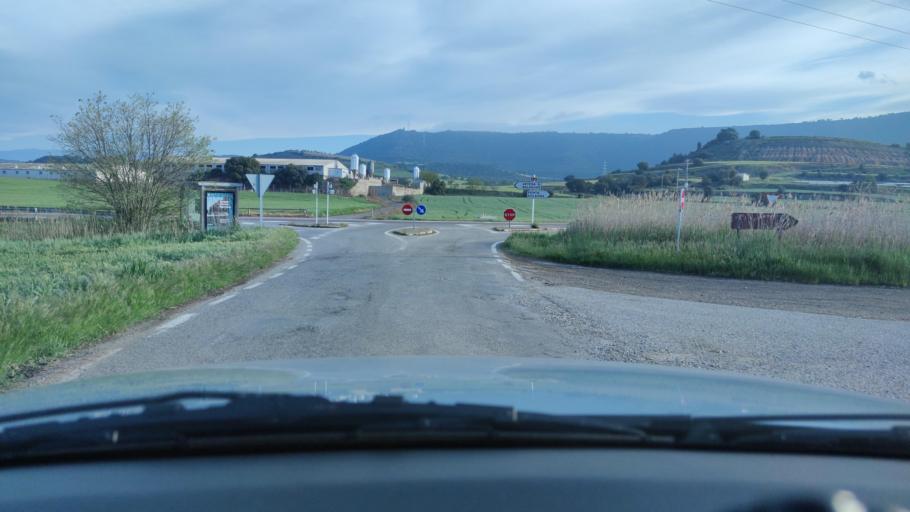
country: ES
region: Catalonia
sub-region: Provincia de Lleida
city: Artesa de Segre
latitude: 41.8810
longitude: 1.1124
